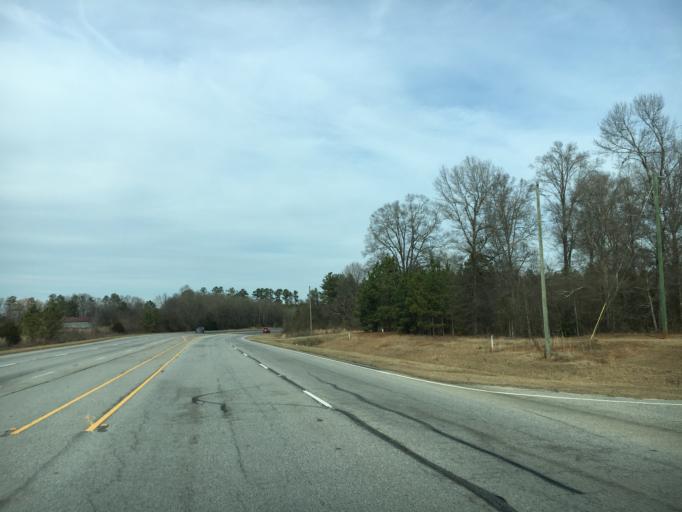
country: US
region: South Carolina
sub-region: Laurens County
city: Clinton
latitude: 34.3626
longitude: -81.9670
